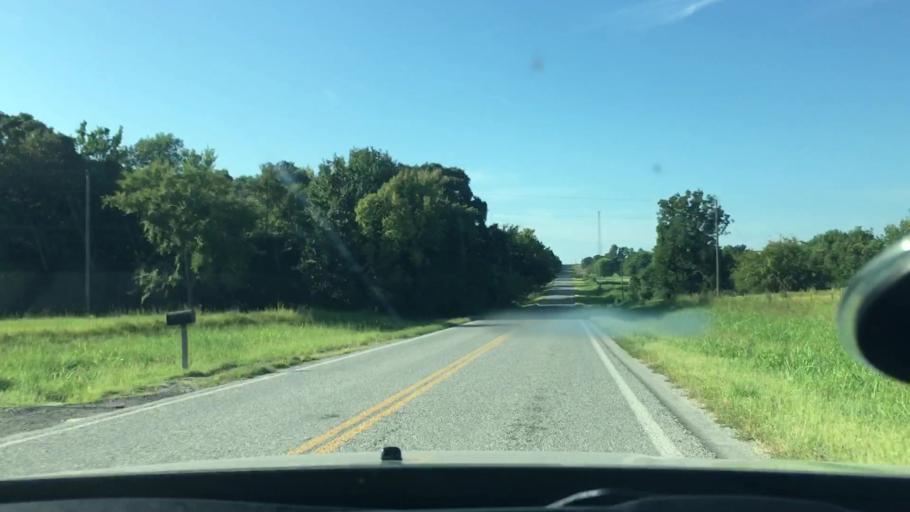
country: US
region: Oklahoma
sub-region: Coal County
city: Coalgate
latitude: 34.6251
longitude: -96.4243
